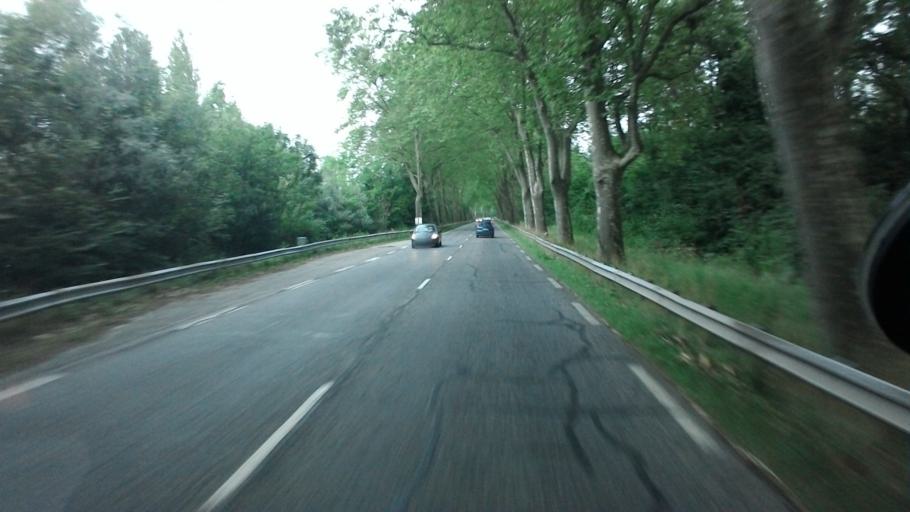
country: FR
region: Rhone-Alpes
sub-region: Departement de la Savoie
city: Cruet
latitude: 45.5111
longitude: 6.0872
